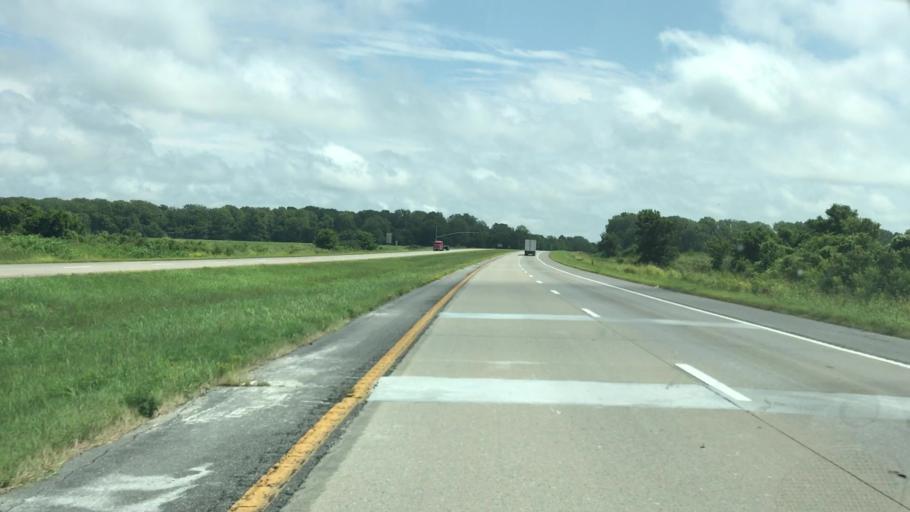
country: US
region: Missouri
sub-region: Pemiscot County
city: Caruthersville
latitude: 36.1386
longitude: -89.6343
